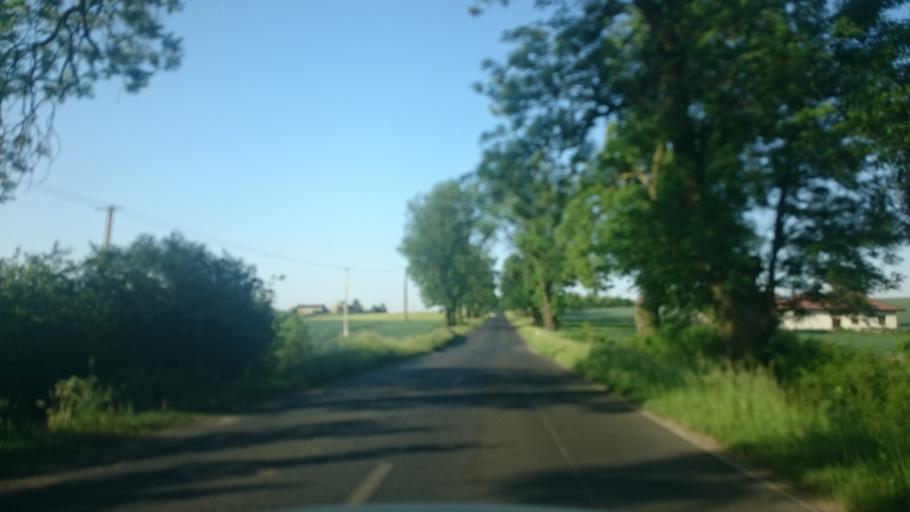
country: PL
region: Kujawsko-Pomorskie
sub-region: Powiat golubsko-dobrzynski
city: Zbojno
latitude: 52.9913
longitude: 19.1244
